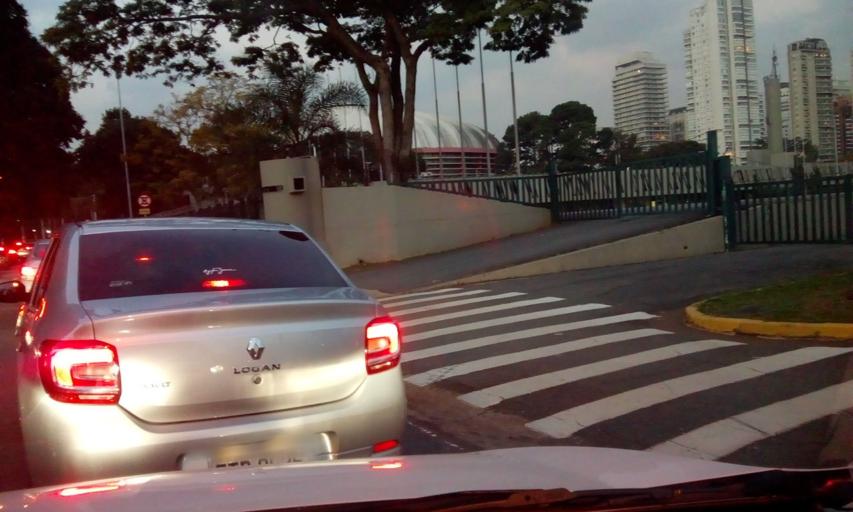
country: BR
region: Sao Paulo
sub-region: Sao Paulo
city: Sao Paulo
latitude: -23.5783
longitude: -46.6587
